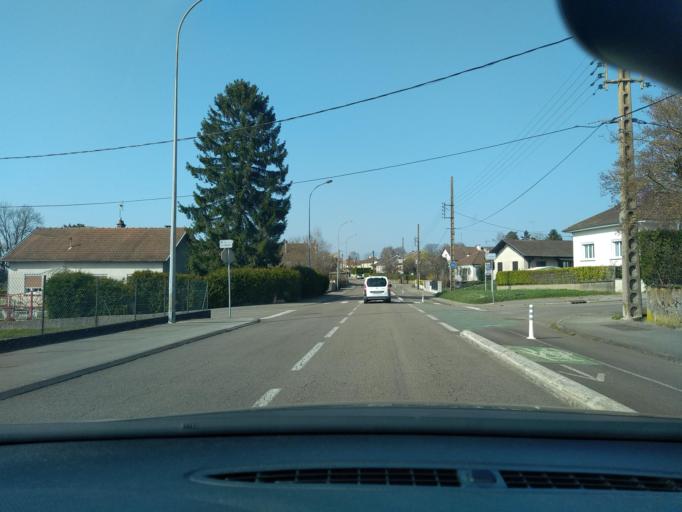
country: FR
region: Franche-Comte
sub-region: Departement du Jura
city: Dole
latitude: 47.0760
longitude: 5.5017
